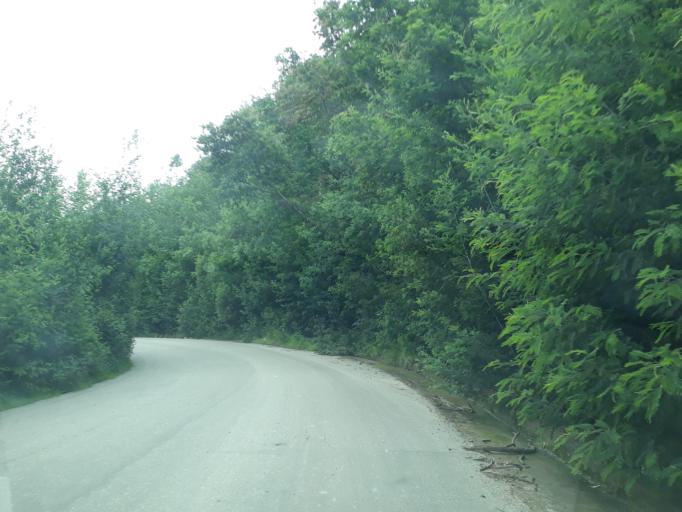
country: CO
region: Cundinamarca
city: Cucunuba
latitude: 5.2234
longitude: -73.7831
